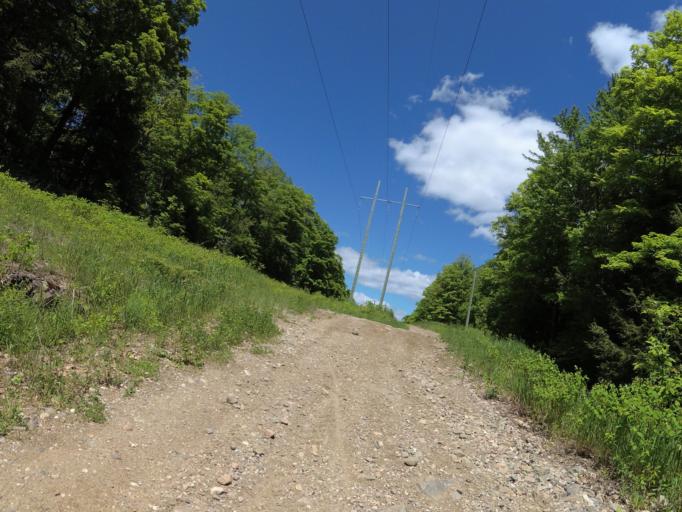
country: CA
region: Ontario
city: Renfrew
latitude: 45.0239
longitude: -76.8876
